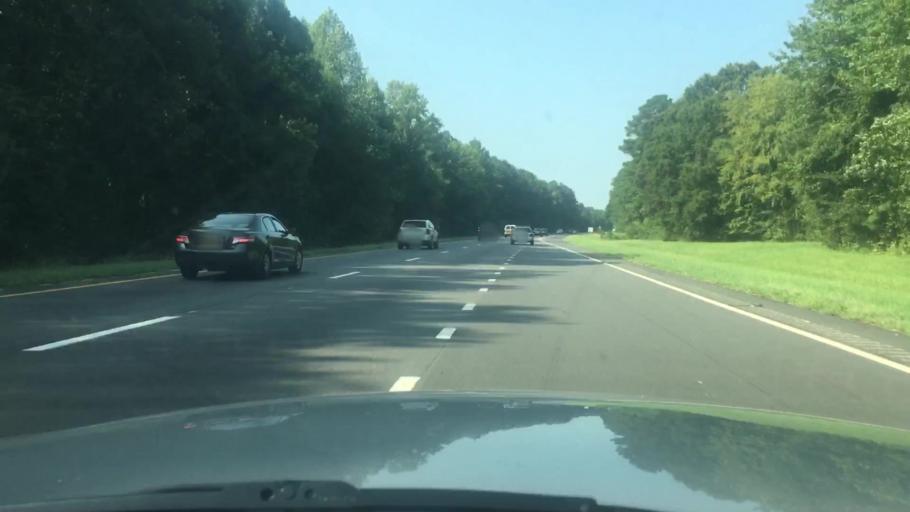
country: US
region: North Carolina
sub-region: Cumberland County
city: Vander
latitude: 35.0030
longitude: -78.8241
